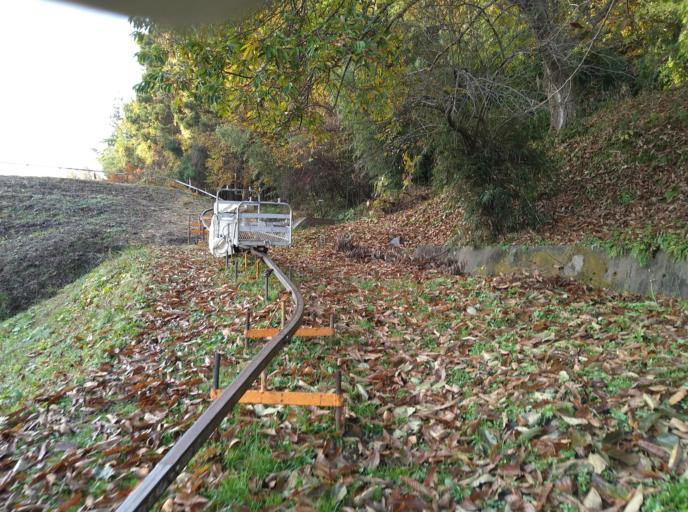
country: JP
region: Iwate
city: Ichinoseki
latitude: 38.9124
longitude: 141.1034
